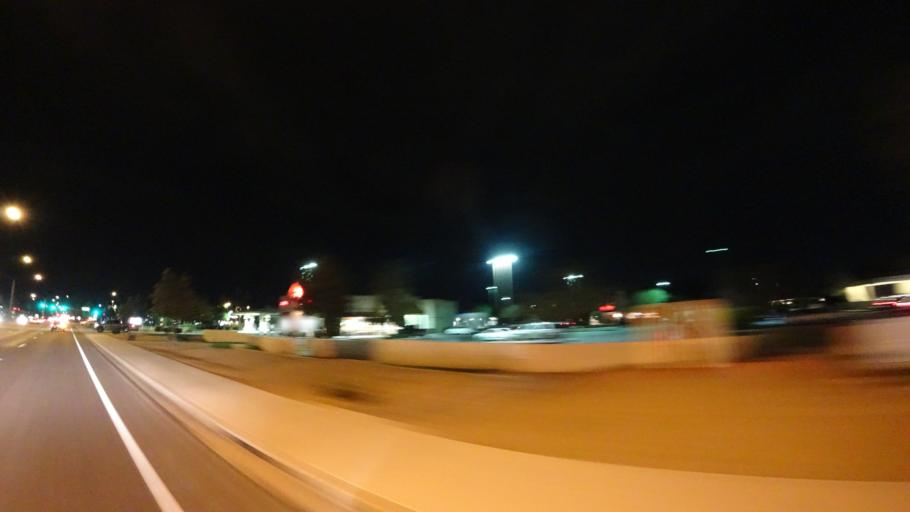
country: US
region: Arizona
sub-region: Maricopa County
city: Gilbert
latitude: 33.3791
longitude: -111.7558
